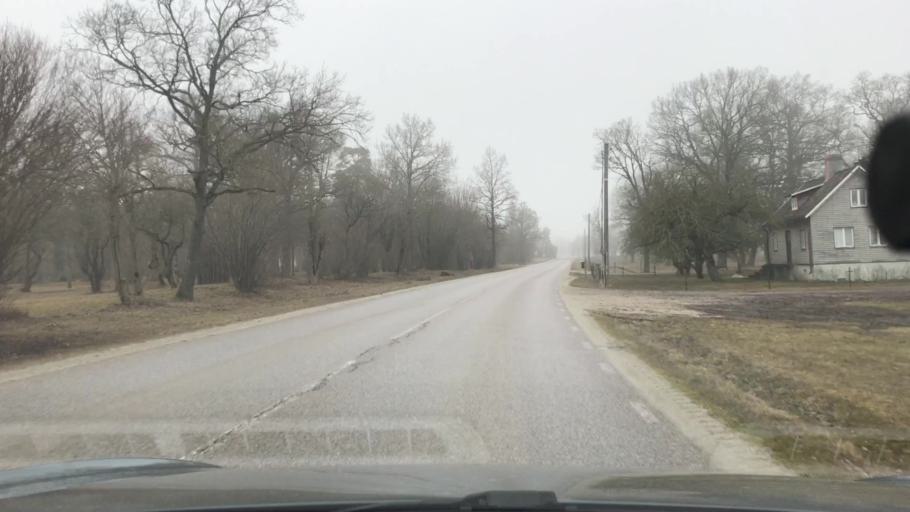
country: SE
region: Gotland
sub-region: Gotland
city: Hemse
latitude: 57.3102
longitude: 18.3804
